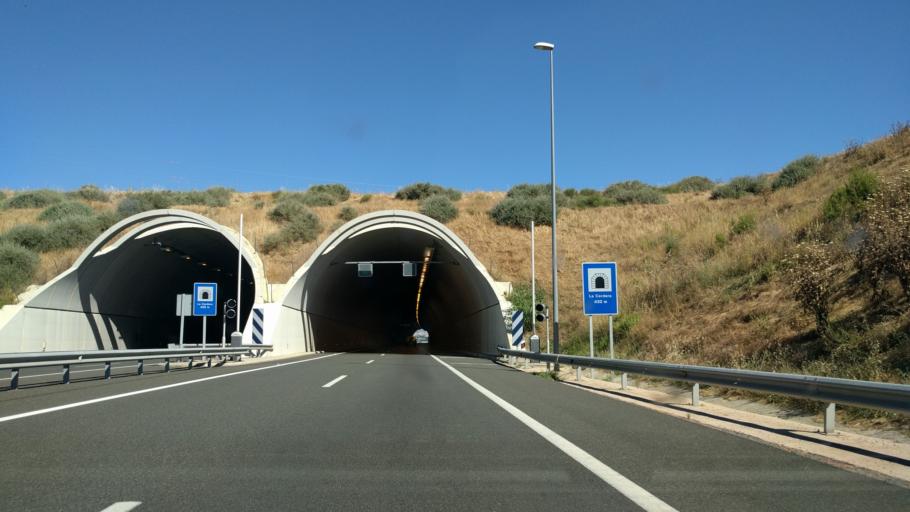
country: ES
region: Catalonia
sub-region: Provincia de Lleida
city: Alpicat
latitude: 41.6643
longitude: 0.5221
